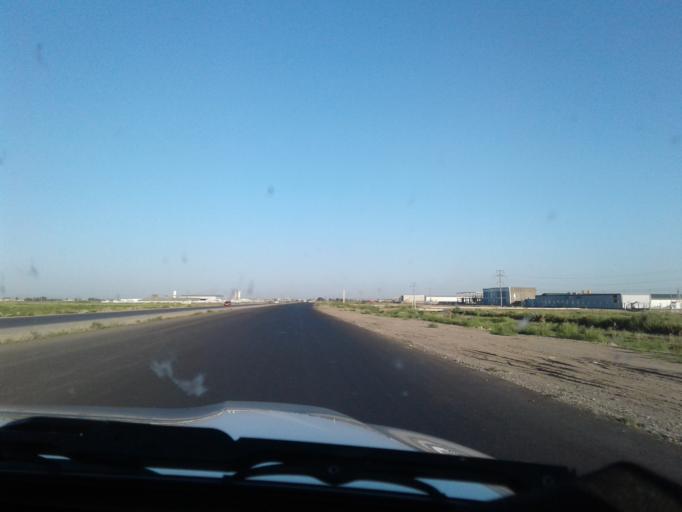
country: TM
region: Mary
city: Mary
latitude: 37.5806
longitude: 61.7936
